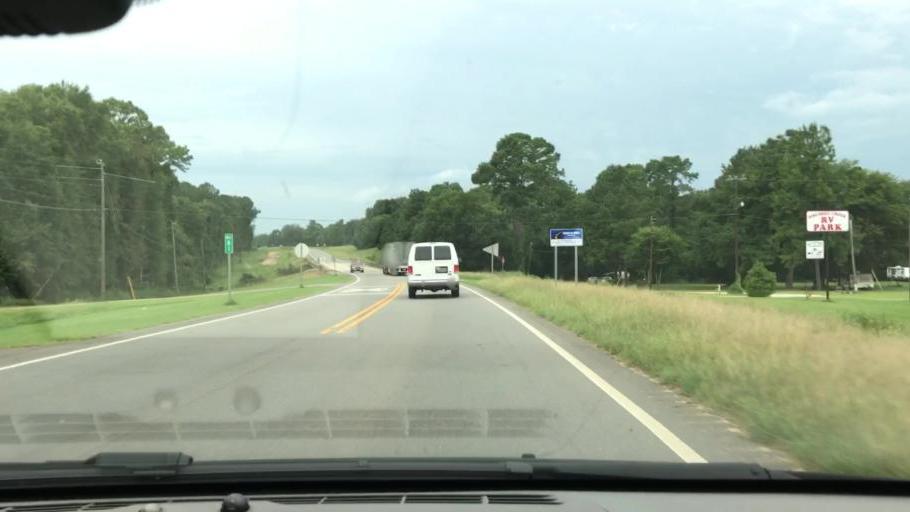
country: US
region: Alabama
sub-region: Houston County
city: Webb
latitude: 31.2934
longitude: -85.1244
